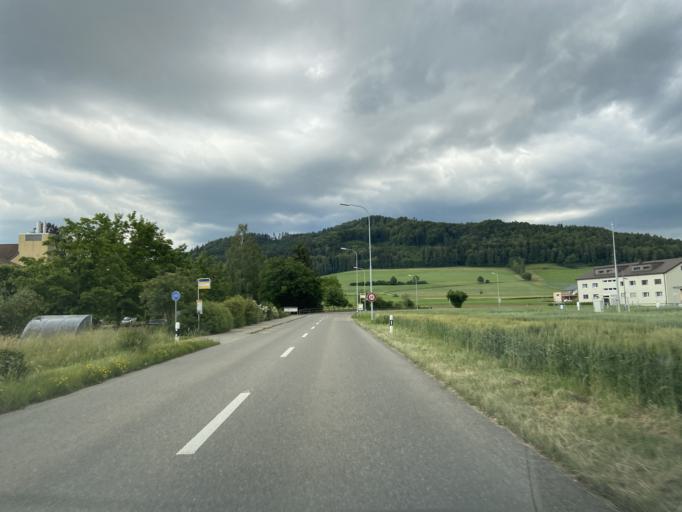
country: CH
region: Thurgau
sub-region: Muenchwilen District
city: Aadorf
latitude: 47.4805
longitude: 8.9053
